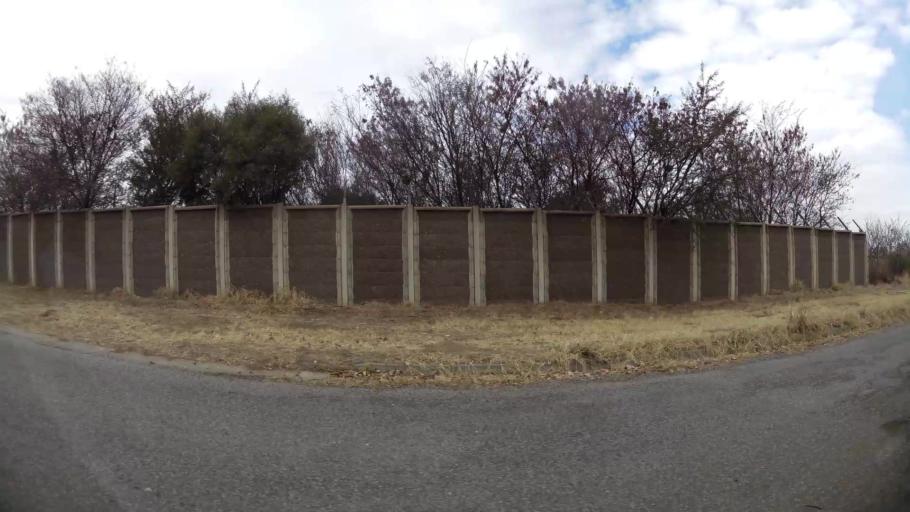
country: ZA
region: Orange Free State
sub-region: Fezile Dabi District Municipality
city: Kroonstad
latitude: -27.6387
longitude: 27.2397
